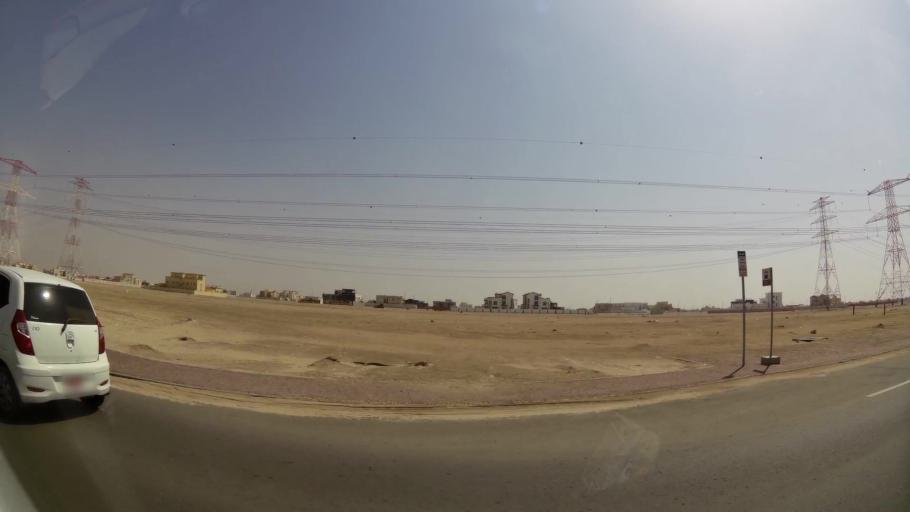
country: AE
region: Abu Dhabi
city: Abu Dhabi
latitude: 24.3071
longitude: 54.5705
